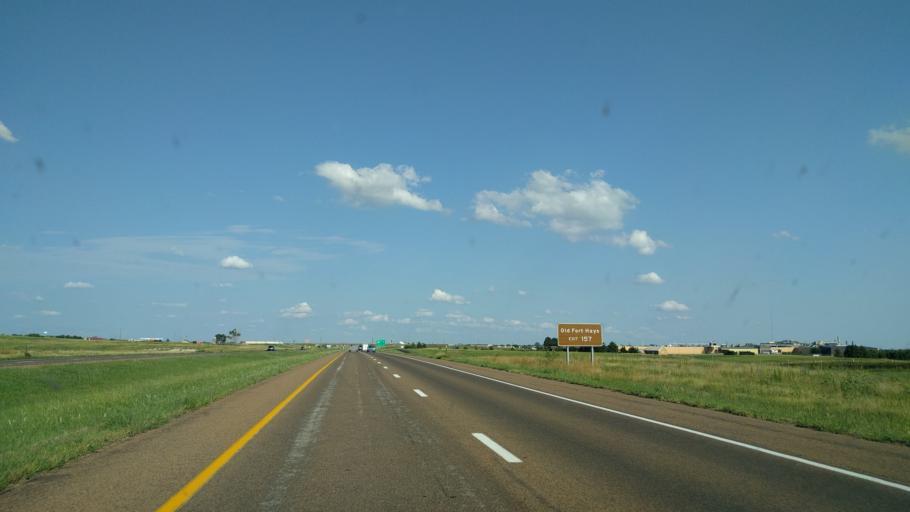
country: US
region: Kansas
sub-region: Ellis County
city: Hays
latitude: 38.9156
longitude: -99.3641
